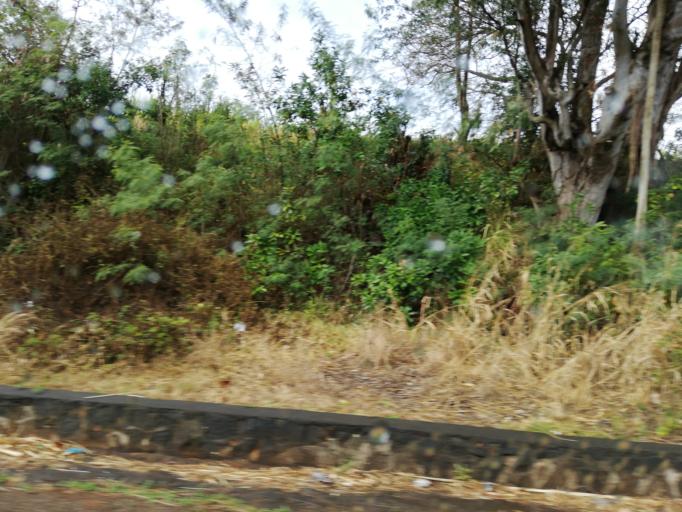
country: MU
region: Pamplemousses
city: Long Mountain
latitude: -20.1258
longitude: 57.5660
